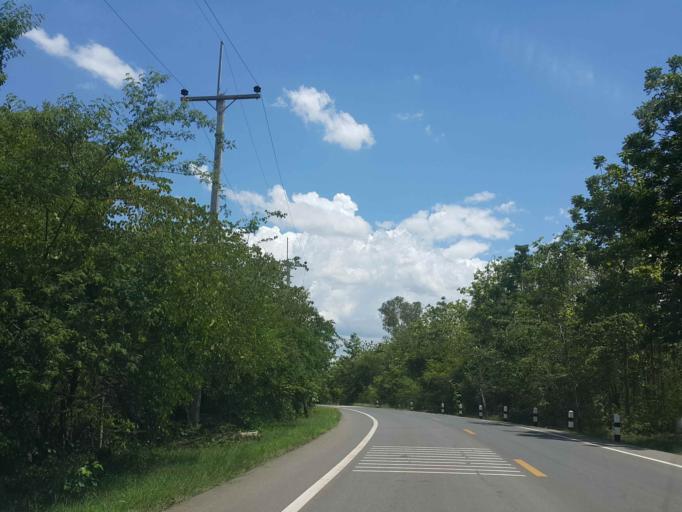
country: TH
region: Phrae
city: Nong Muang Khai
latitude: 18.1869
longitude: 100.2119
